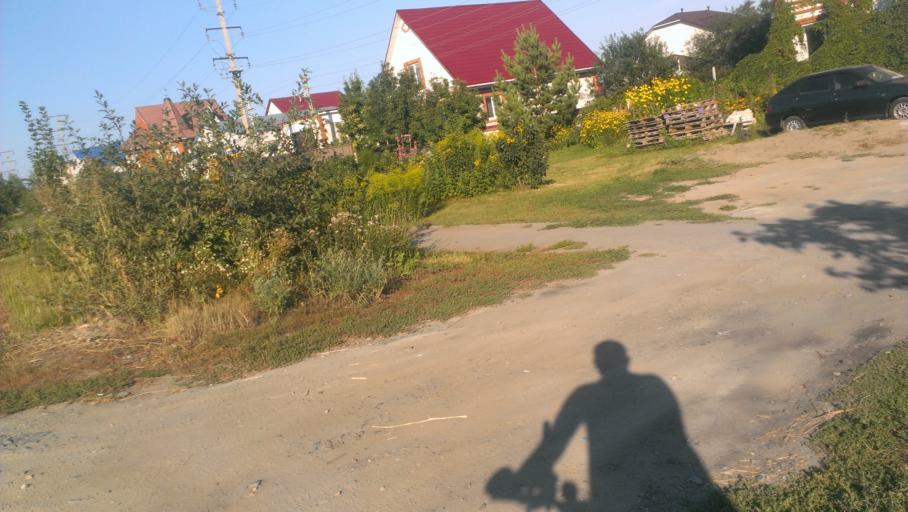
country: RU
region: Altai Krai
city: Novosilikatnyy
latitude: 53.3548
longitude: 83.6349
